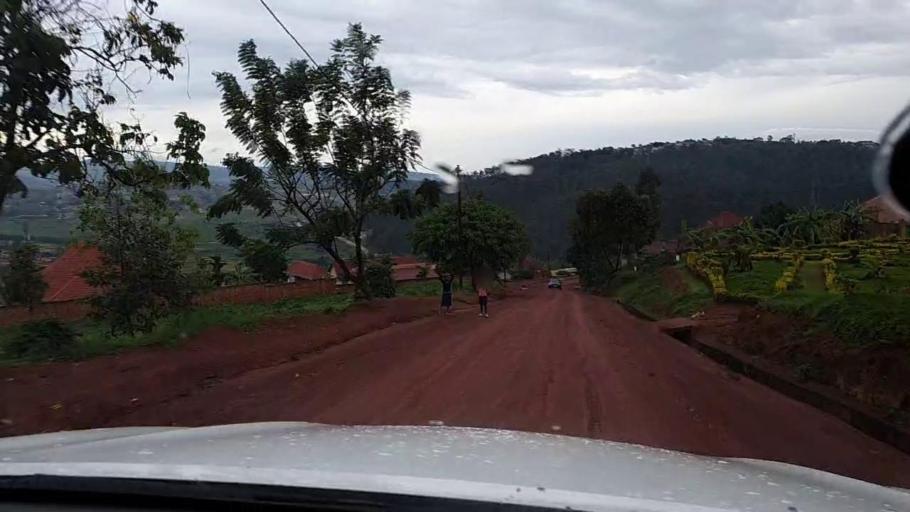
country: RW
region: Kigali
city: Kigali
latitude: -1.9040
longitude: 30.0441
